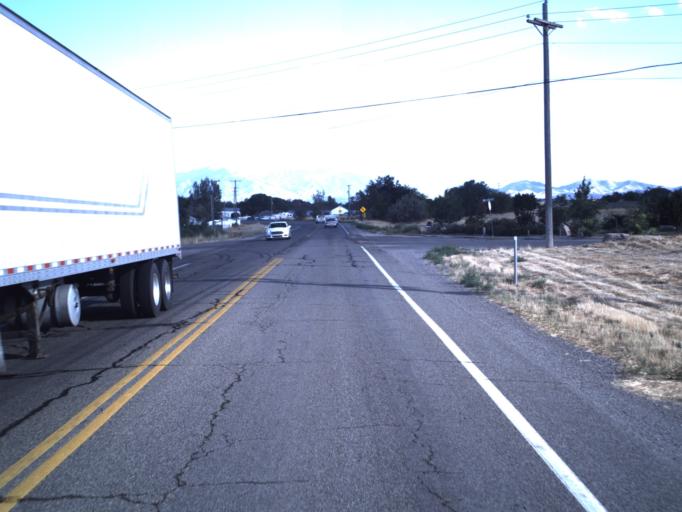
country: US
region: Utah
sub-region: Tooele County
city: Grantsville
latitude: 40.6027
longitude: -112.4851
